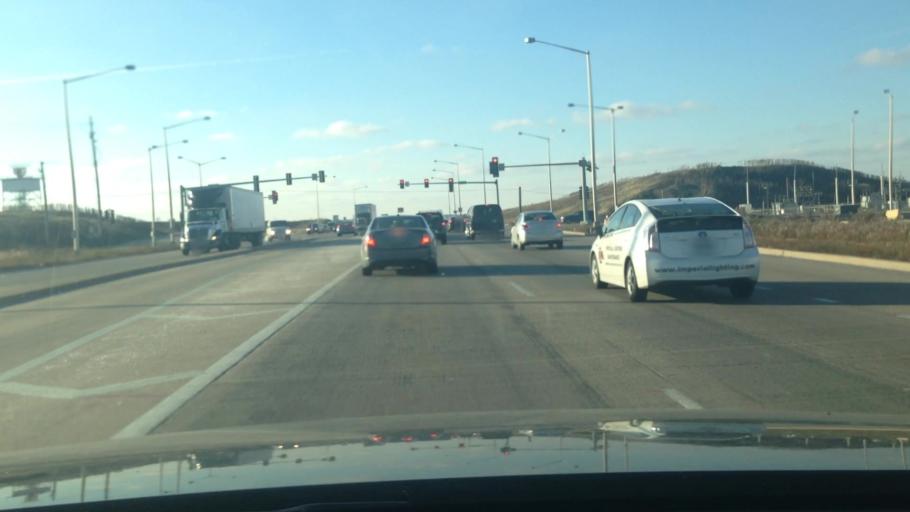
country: US
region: Illinois
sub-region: DuPage County
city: Bensenville
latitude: 41.9531
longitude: -87.9128
